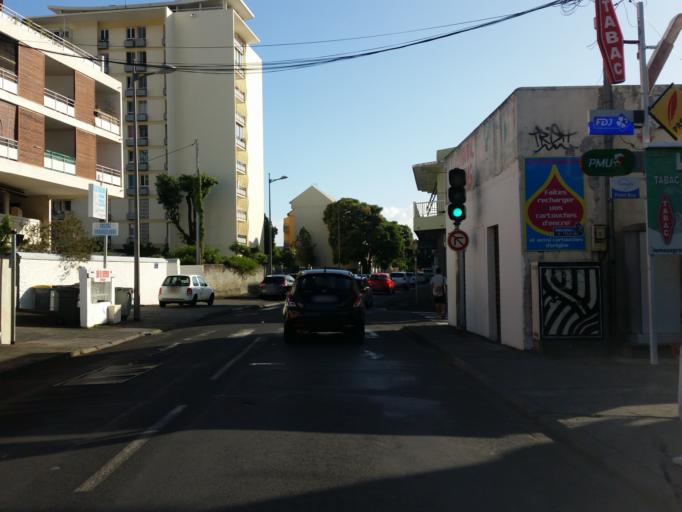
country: RE
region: Reunion
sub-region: Reunion
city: Saint-Denis
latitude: -20.8891
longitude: 55.4550
